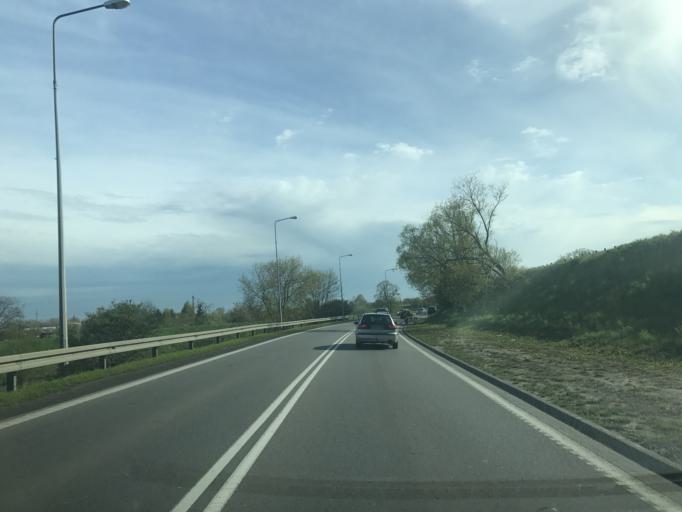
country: PL
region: Pomeranian Voivodeship
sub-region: Powiat gdanski
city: Pruszcz Gdanski
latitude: 54.2770
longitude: 18.6398
